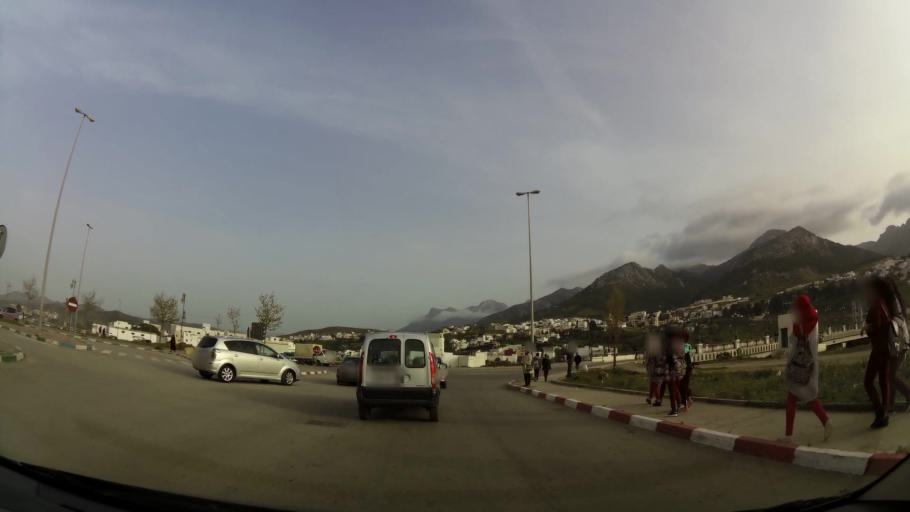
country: MA
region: Tanger-Tetouan
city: Tetouan
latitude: 35.5600
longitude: -5.3723
